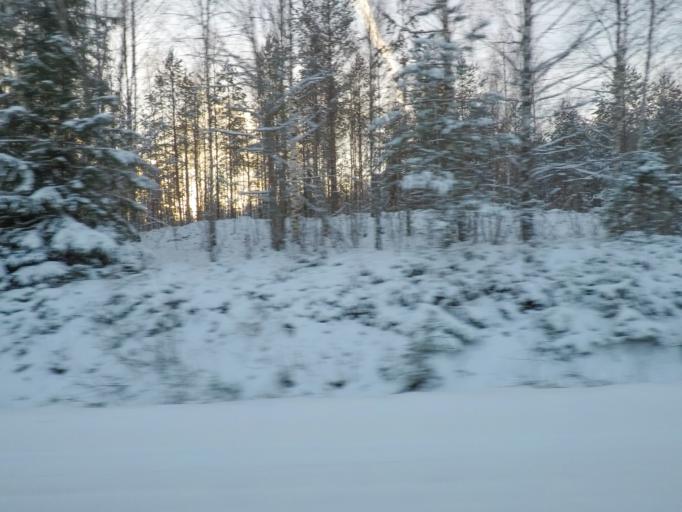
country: FI
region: Varsinais-Suomi
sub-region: Salo
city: Suomusjaervi
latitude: 60.3085
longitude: 23.6456
